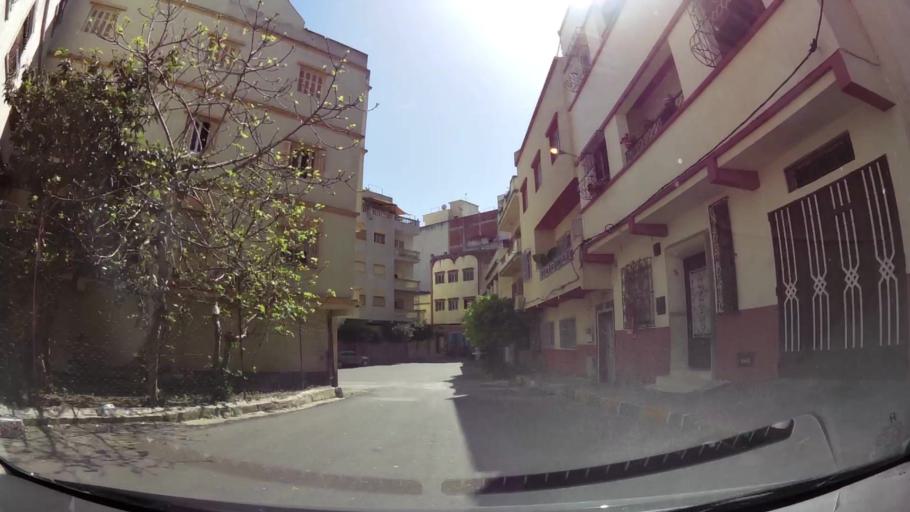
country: MA
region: Tanger-Tetouan
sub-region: Tanger-Assilah
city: Tangier
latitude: 35.7499
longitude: -5.8133
